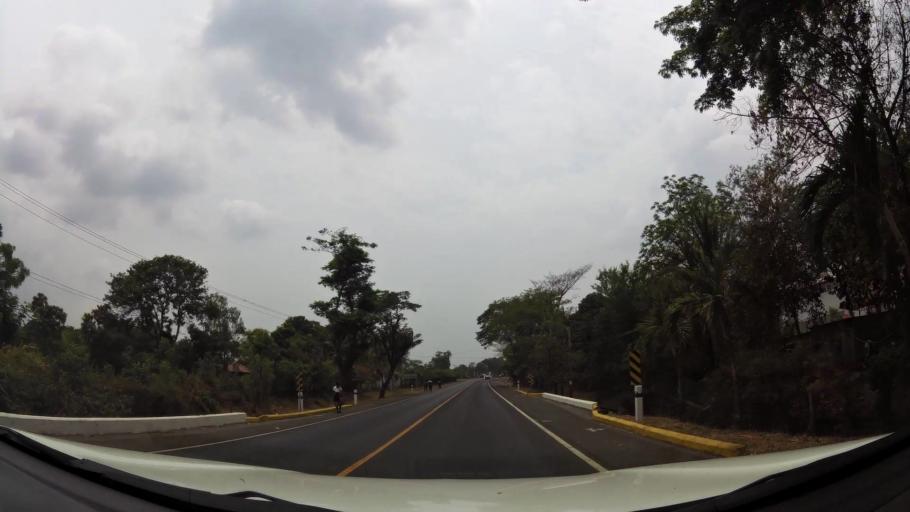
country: NI
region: Leon
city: Quezalguaque
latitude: 12.5339
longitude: -86.8981
